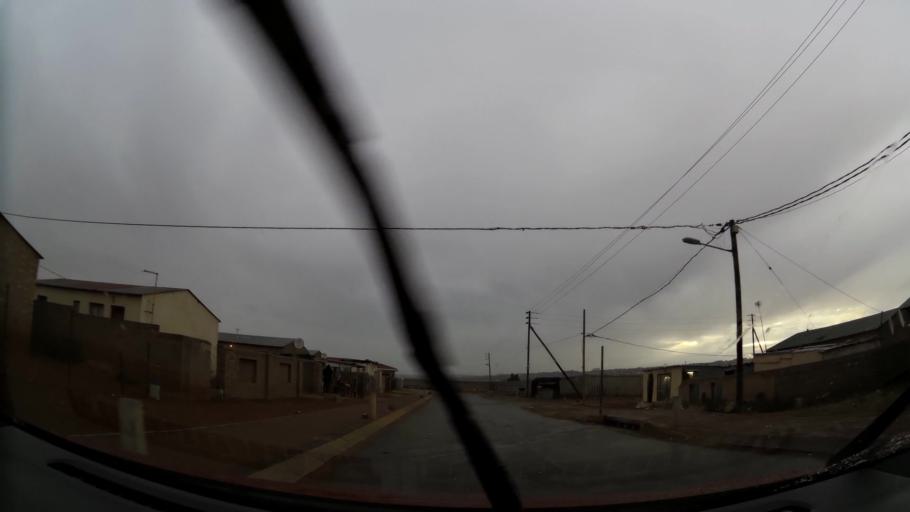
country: ZA
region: Gauteng
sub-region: West Rand District Municipality
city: Randfontein
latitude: -26.1746
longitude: 27.7856
